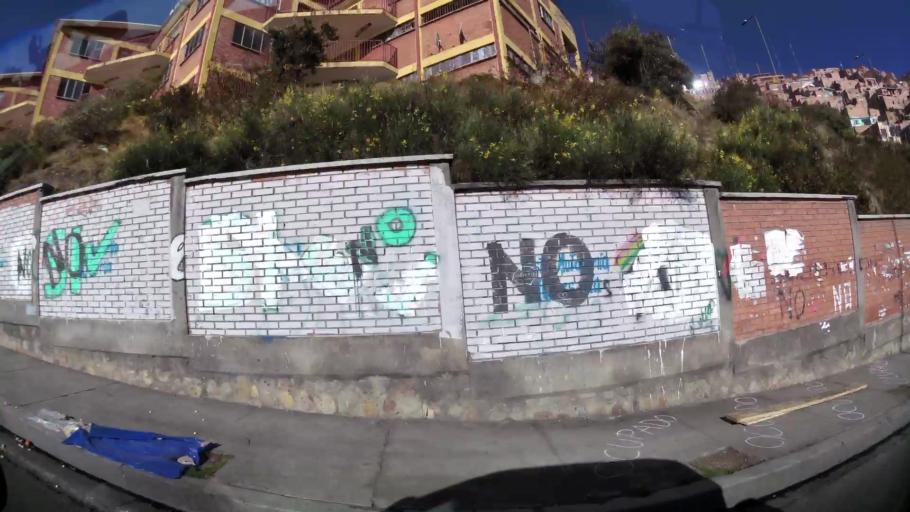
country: BO
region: La Paz
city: La Paz
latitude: -16.5095
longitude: -68.1521
